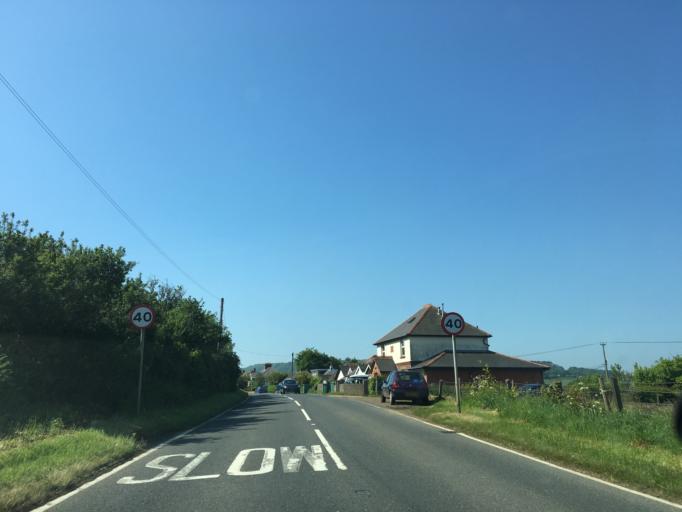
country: GB
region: England
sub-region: Isle of Wight
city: Newchurch
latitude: 50.6342
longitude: -1.2200
